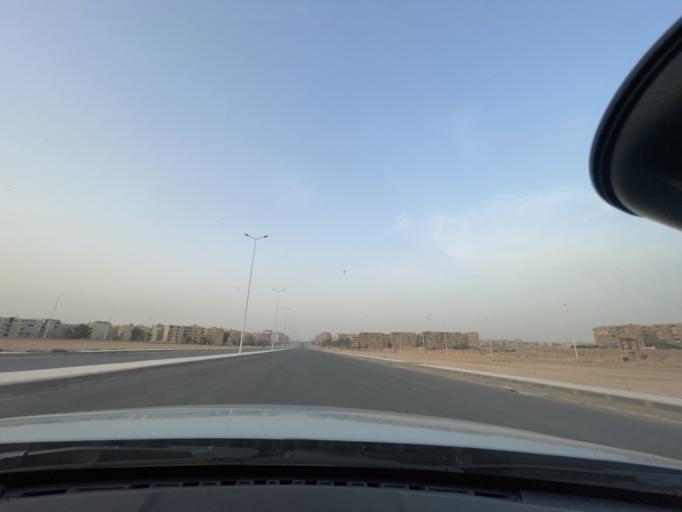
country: EG
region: Muhafazat al Qahirah
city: Cairo
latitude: 30.0410
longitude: 31.3598
